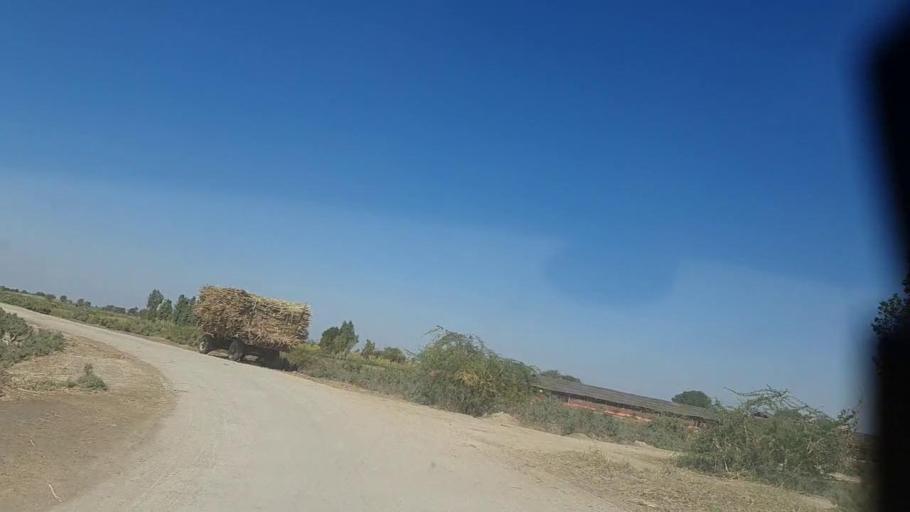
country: PK
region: Sindh
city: Digri
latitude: 25.1685
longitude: 69.0504
